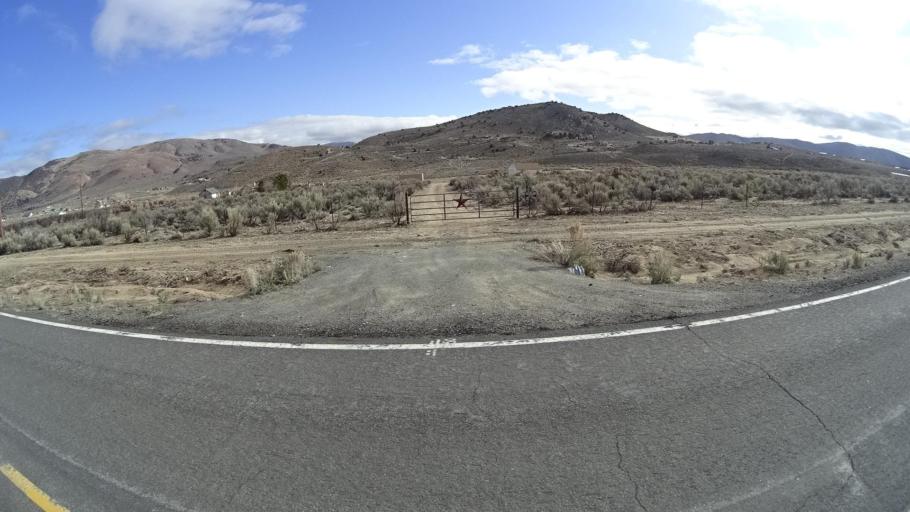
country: US
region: Nevada
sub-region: Washoe County
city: Cold Springs
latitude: 39.8799
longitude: -119.9669
